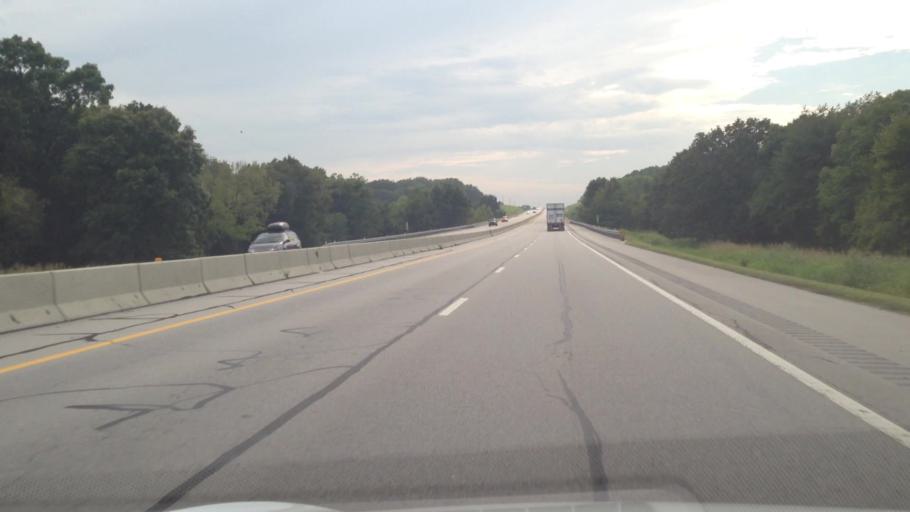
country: US
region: Kansas
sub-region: Cherokee County
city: Baxter Springs
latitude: 36.9270
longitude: -94.7377
